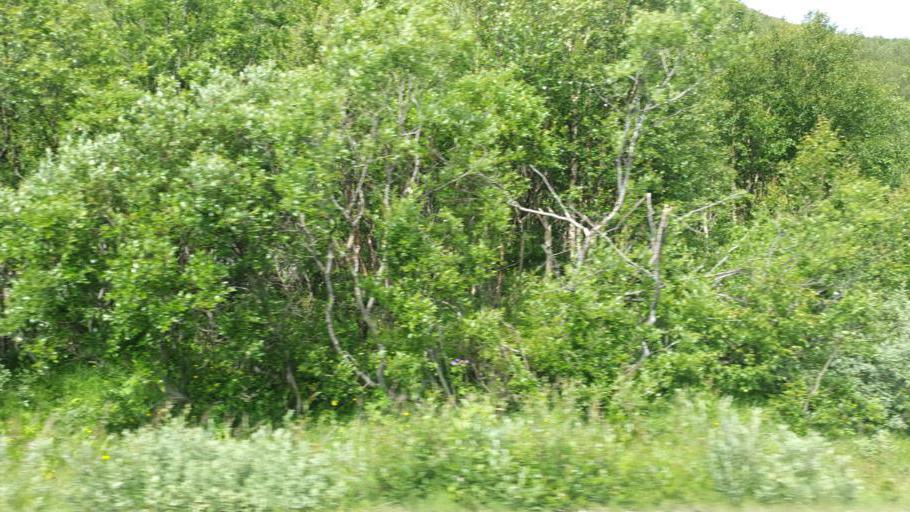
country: NO
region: Oppland
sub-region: Vaga
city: Vagamo
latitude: 61.5266
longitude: 8.8750
